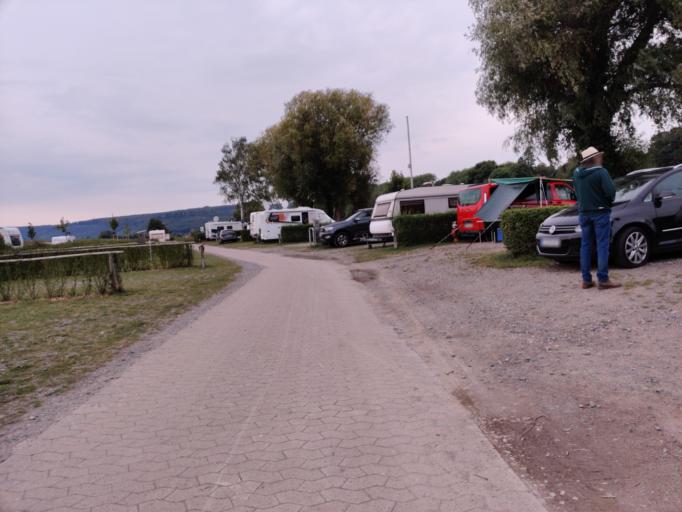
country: DE
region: Lower Saxony
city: Hehlen
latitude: 52.0181
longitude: 9.4261
